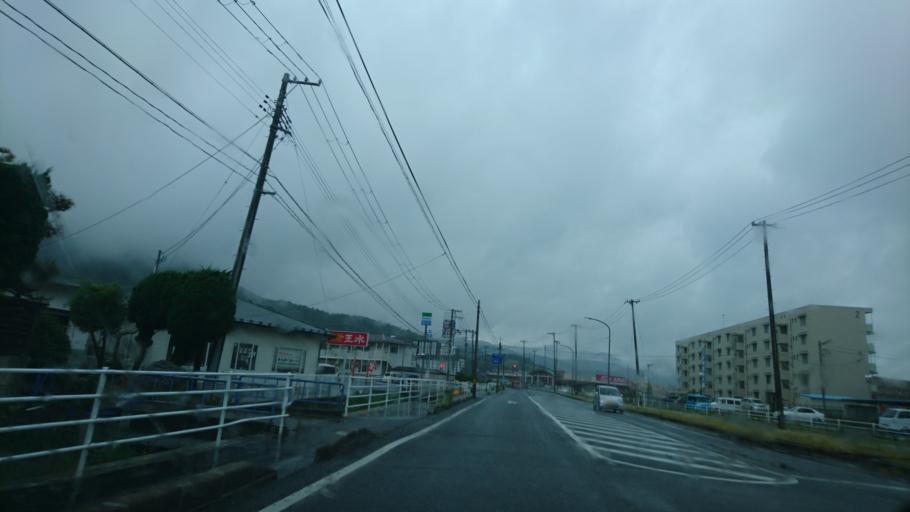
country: JP
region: Miyagi
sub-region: Oshika Gun
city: Onagawa Cho
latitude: 38.4264
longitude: 141.3721
